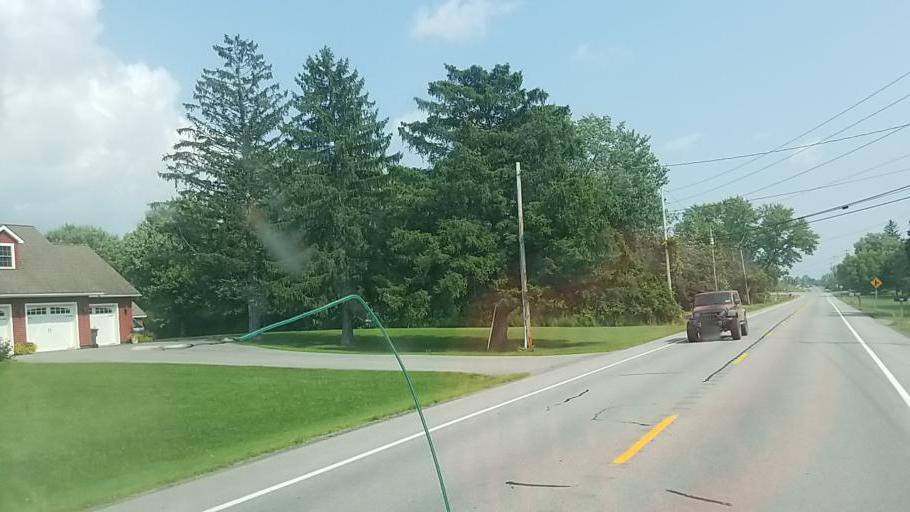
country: US
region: New York
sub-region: Fulton County
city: Johnstown
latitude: 42.9909
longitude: -74.3323
